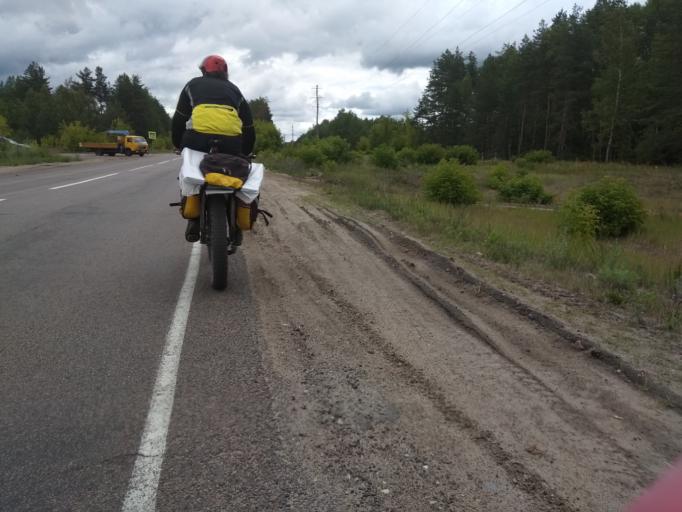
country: RU
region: Moskovskaya
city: Kerva
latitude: 55.5787
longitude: 39.6882
